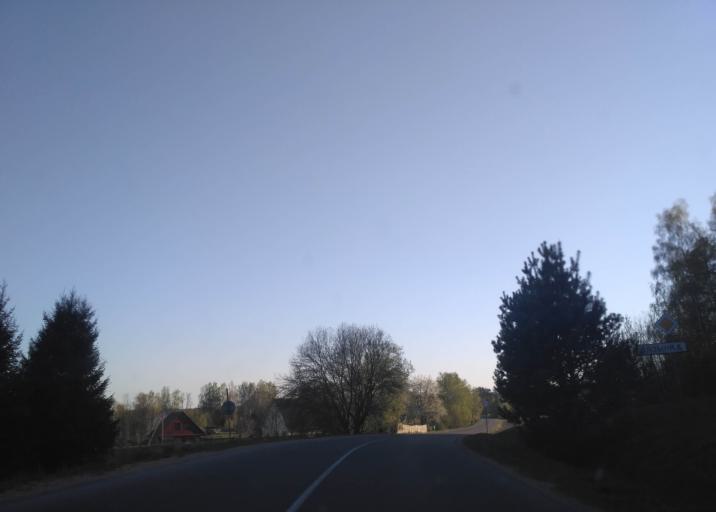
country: BY
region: Minsk
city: Radashkovichy
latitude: 54.1212
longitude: 27.1992
